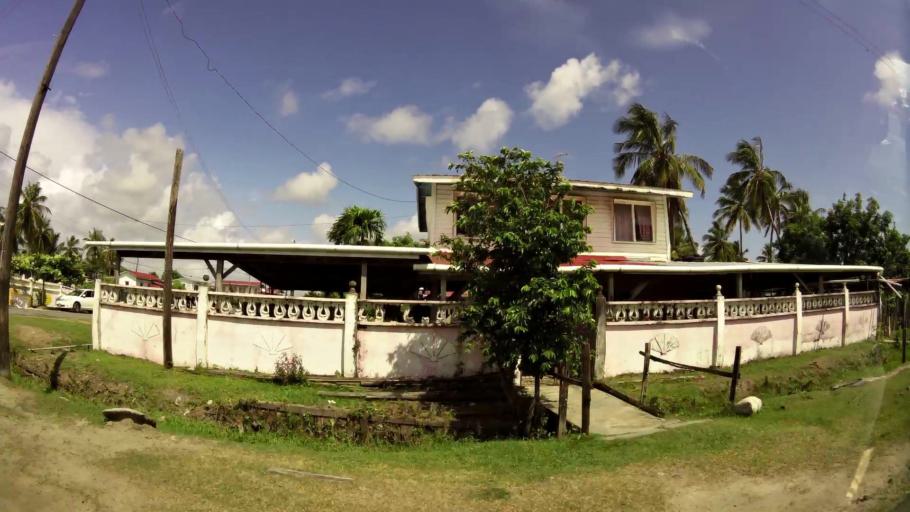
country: GY
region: Demerara-Mahaica
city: Mahaica Village
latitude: 6.7537
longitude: -57.9950
